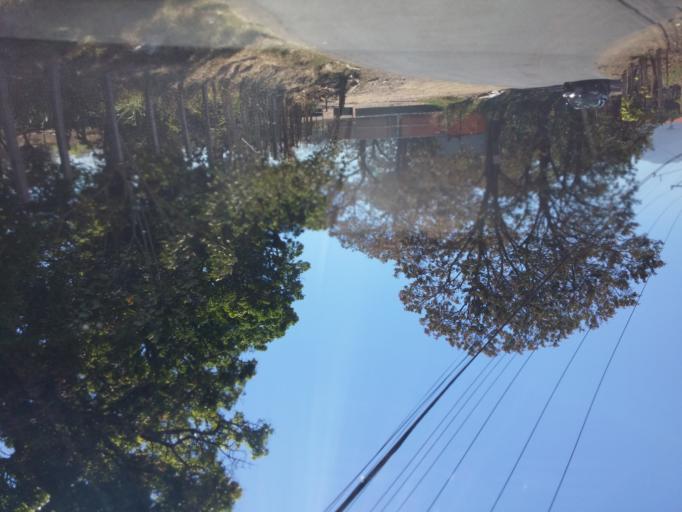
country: CR
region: Alajuela
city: Alajuela
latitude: 9.9990
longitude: -84.2346
